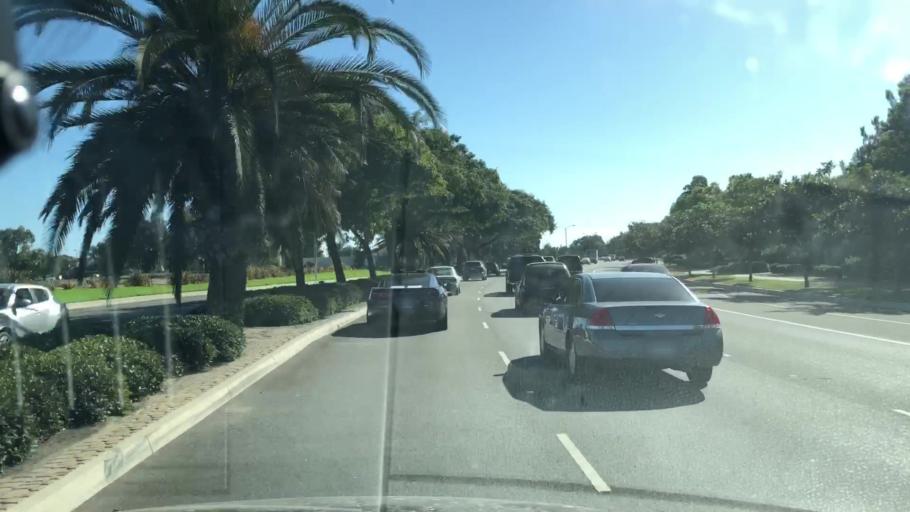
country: US
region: California
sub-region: Ventura County
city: El Rio
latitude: 34.2170
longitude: -119.1584
